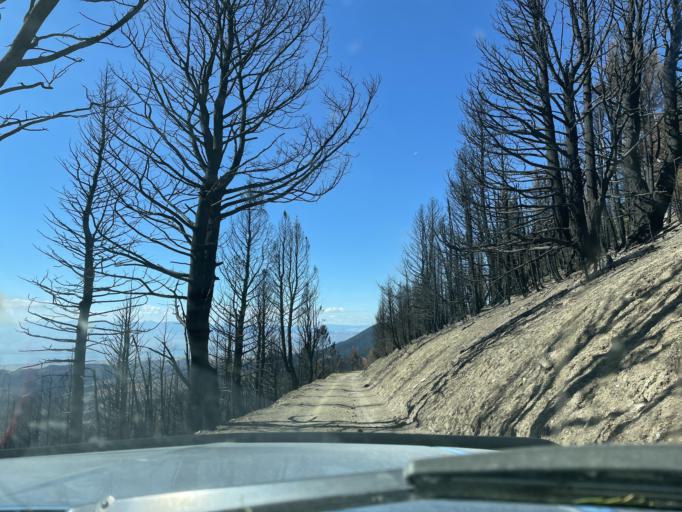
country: US
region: Montana
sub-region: Broadwater County
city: Townsend
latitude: 46.5015
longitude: -111.2736
